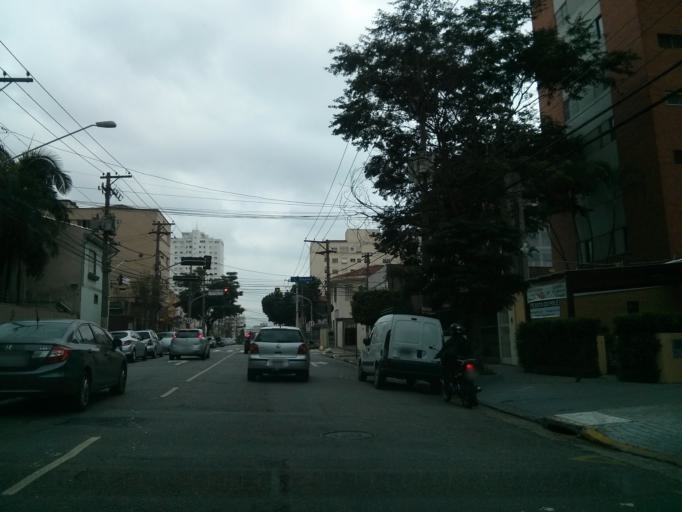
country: BR
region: Sao Paulo
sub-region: Sao Paulo
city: Sao Paulo
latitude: -23.6014
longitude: -46.6463
